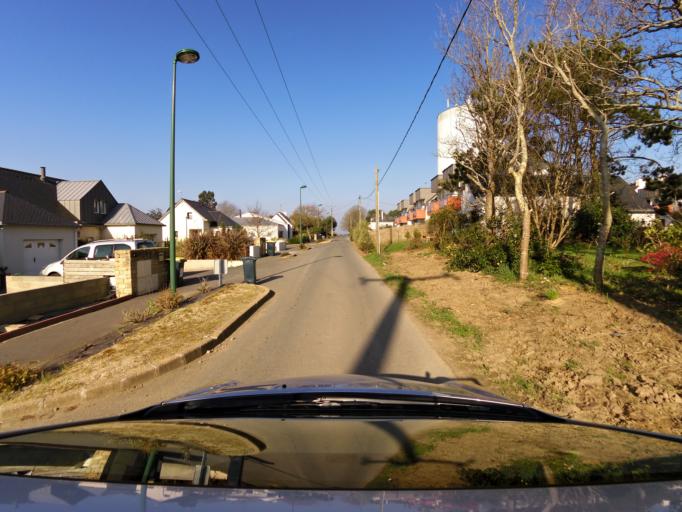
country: FR
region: Brittany
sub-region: Departement du Morbihan
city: Guidel-Plage
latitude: 47.7748
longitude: -3.5145
